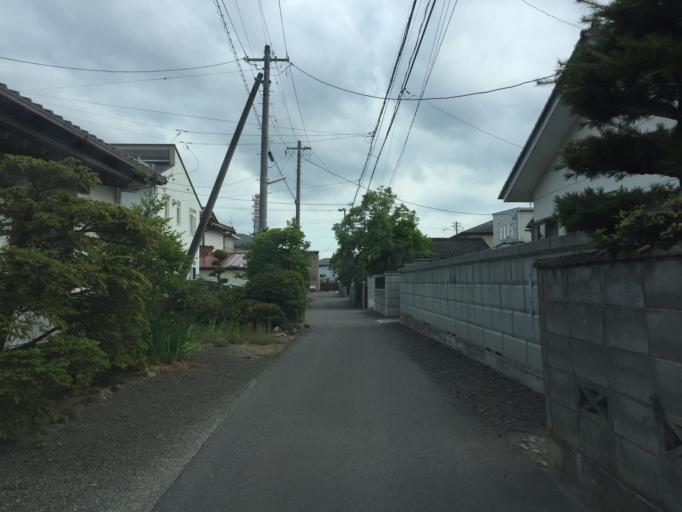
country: JP
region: Fukushima
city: Fukushima-shi
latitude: 37.7496
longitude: 140.4430
